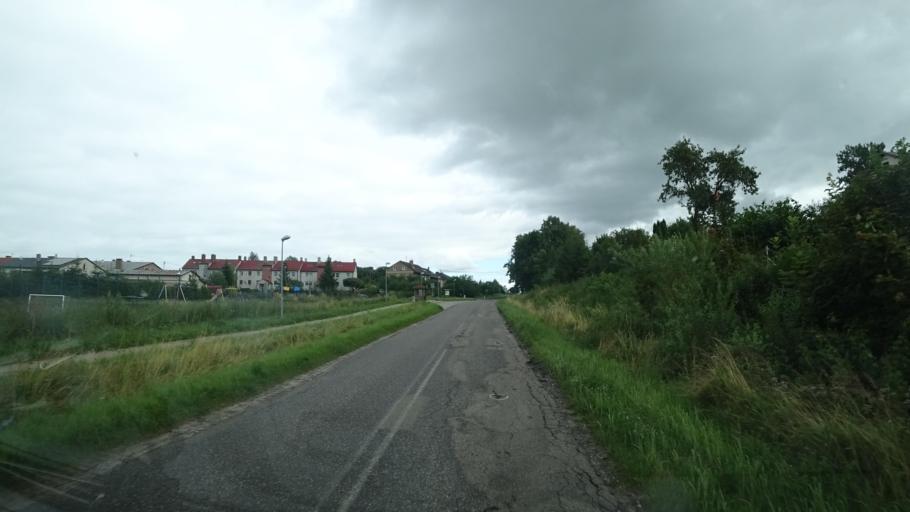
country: PL
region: Warmian-Masurian Voivodeship
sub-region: Powiat goldapski
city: Goldap
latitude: 54.3050
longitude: 22.4228
